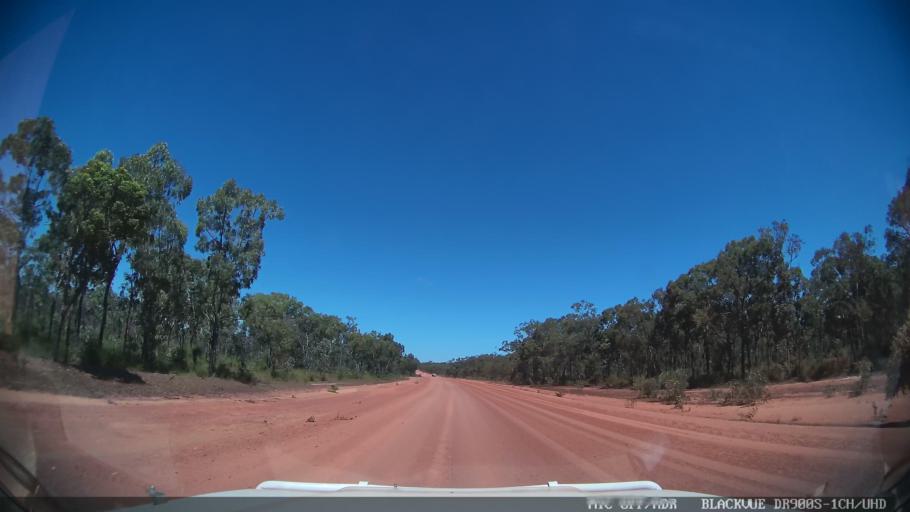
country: AU
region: Queensland
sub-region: Torres
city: Thursday Island
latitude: -11.3641
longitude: 142.3459
